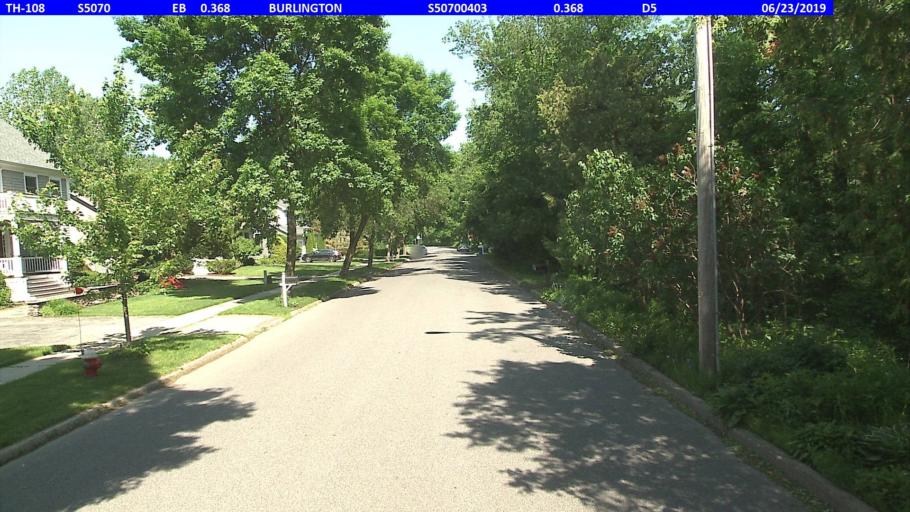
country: US
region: Vermont
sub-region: Chittenden County
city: Burlington
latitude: 44.5052
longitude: -73.2655
